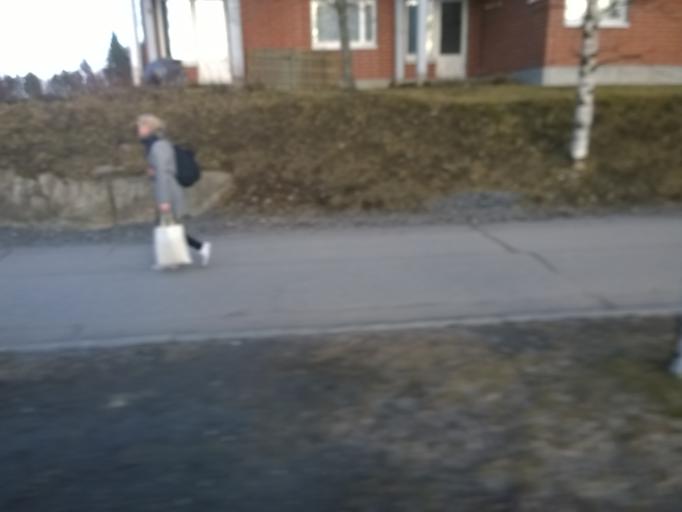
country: FI
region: Pirkanmaa
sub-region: Tampere
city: Tampere
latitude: 61.4553
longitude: 23.8500
